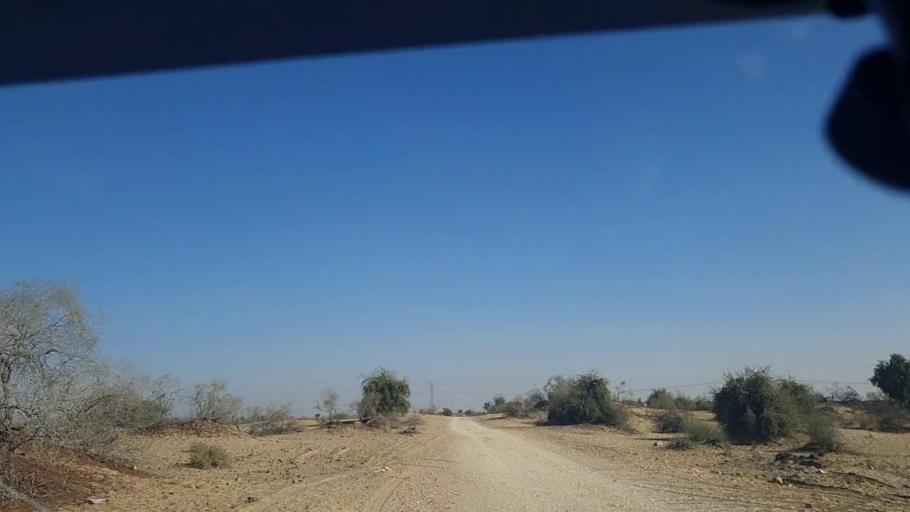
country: PK
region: Sindh
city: Khanpur
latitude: 27.6473
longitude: 69.3955
